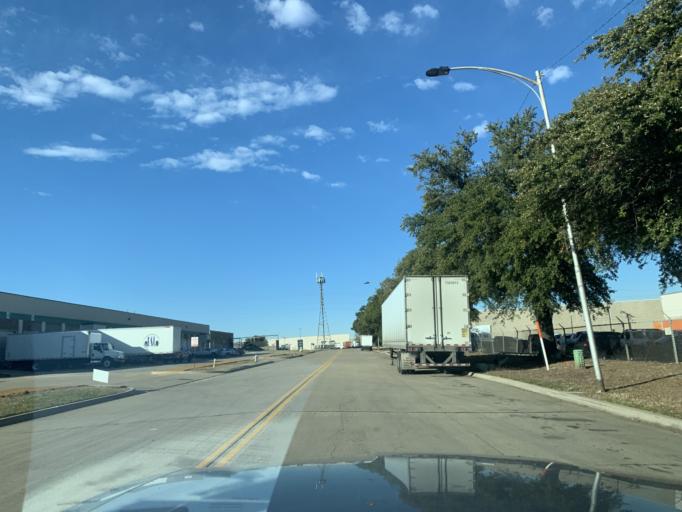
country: US
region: Texas
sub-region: Tarrant County
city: Arlington
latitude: 32.7445
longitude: -97.0709
